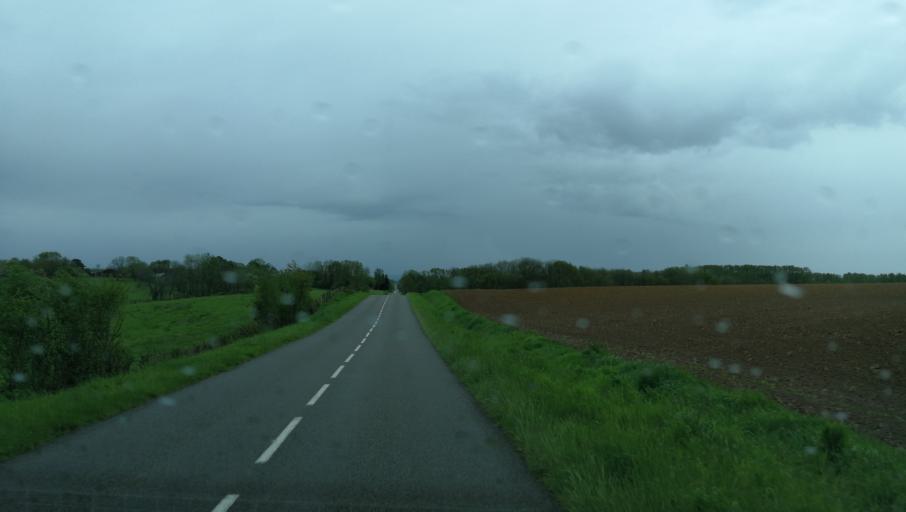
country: FR
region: Franche-Comte
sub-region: Departement du Jura
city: Bletterans
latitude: 46.8016
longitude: 5.4015
